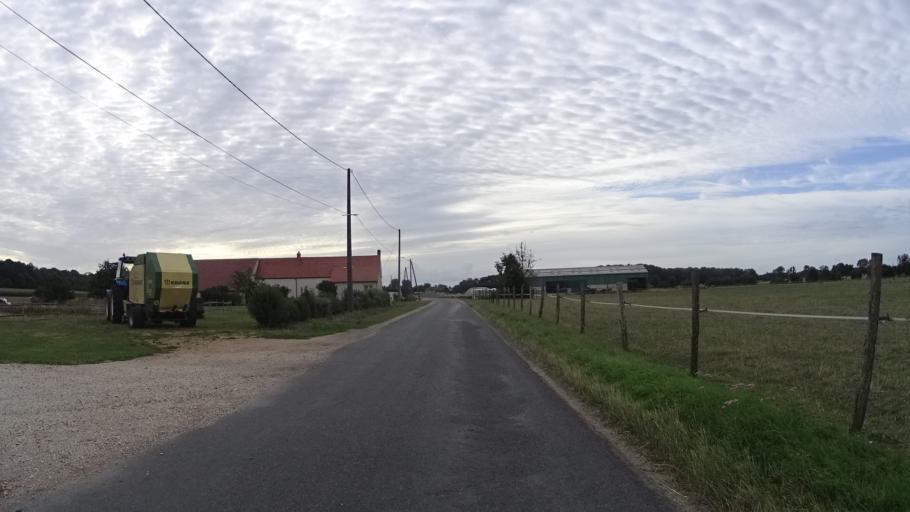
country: FR
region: Centre
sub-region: Departement du Loiret
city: Saint-Benoit-sur-Loire
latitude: 47.8424
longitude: 2.3073
